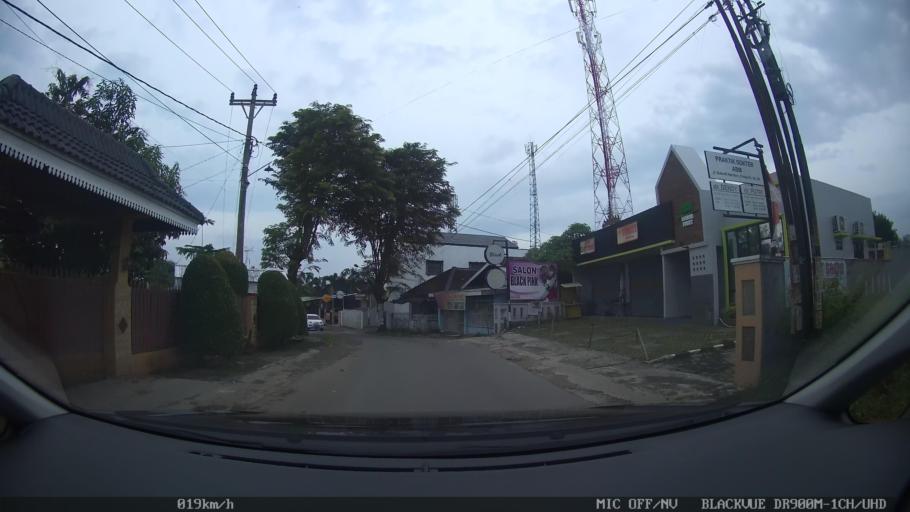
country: ID
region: Lampung
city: Kedaton
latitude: -5.3845
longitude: 105.2493
